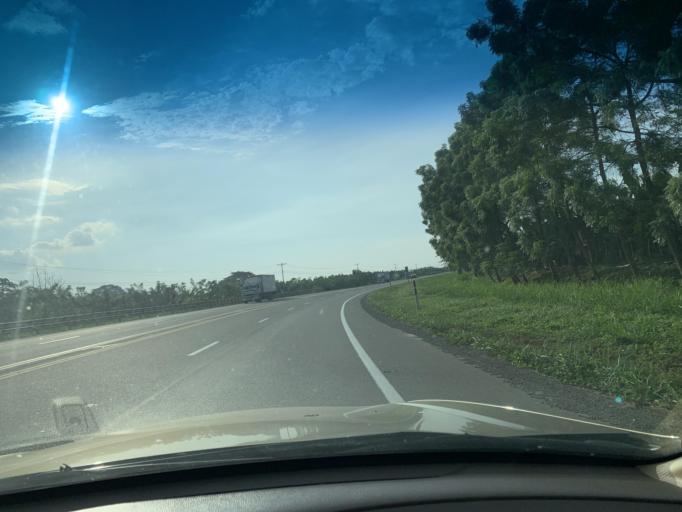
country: EC
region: Guayas
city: Coronel Marcelino Mariduena
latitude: -2.2792
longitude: -79.5307
